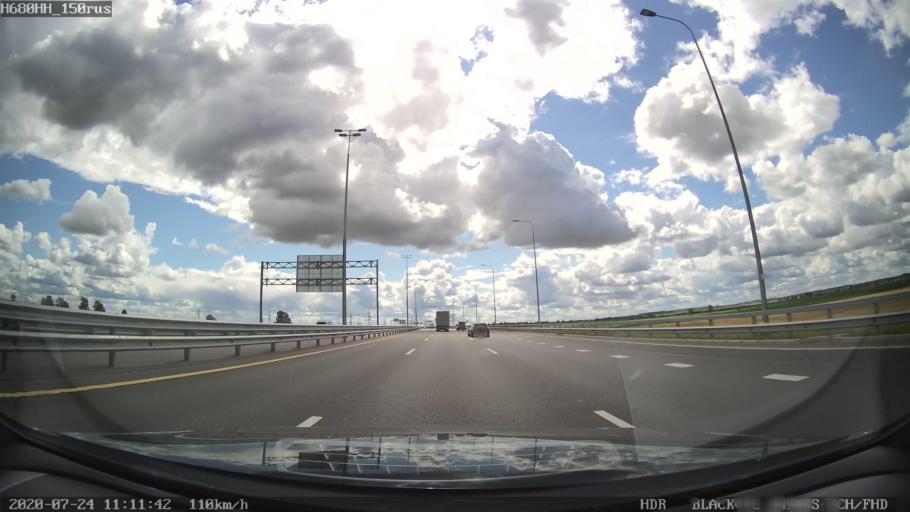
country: RU
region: Leningrad
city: Fedorovskoye
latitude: 59.7191
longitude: 30.5199
